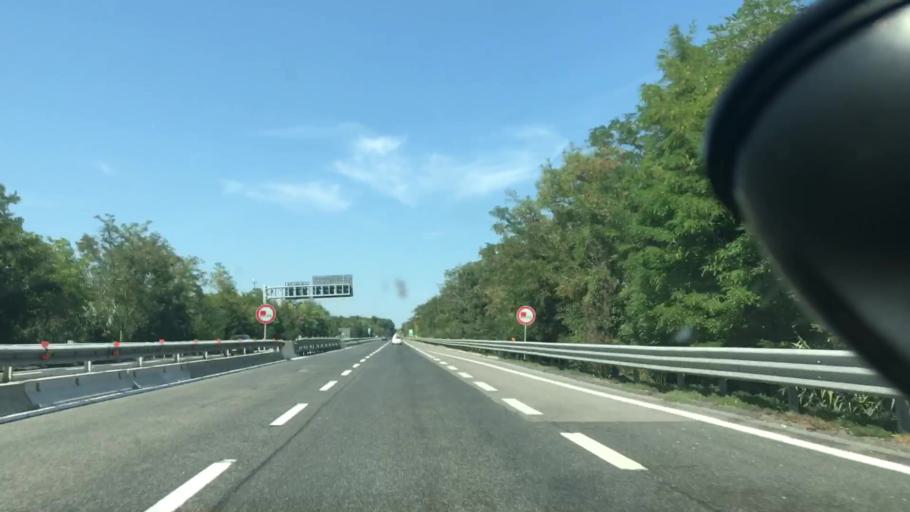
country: IT
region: Abruzzo
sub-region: Provincia di Chieti
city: Casalbordino-Miracoli
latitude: 42.1606
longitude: 14.6376
